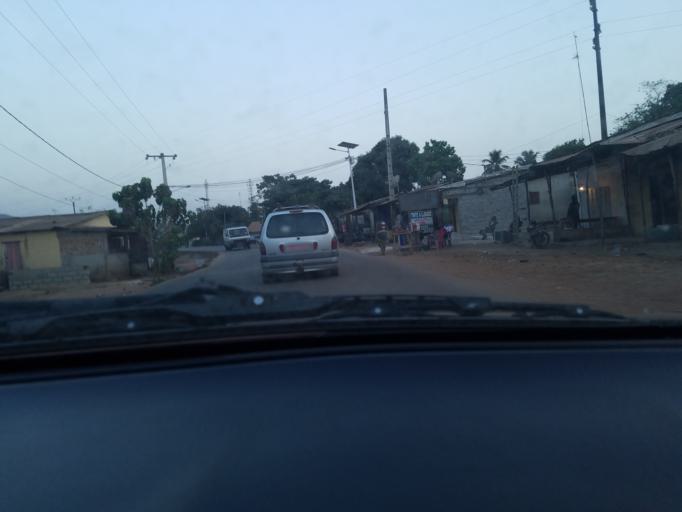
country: GN
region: Kindia
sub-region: Prefecture de Dubreka
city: Dubreka
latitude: 9.7885
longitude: -13.4887
